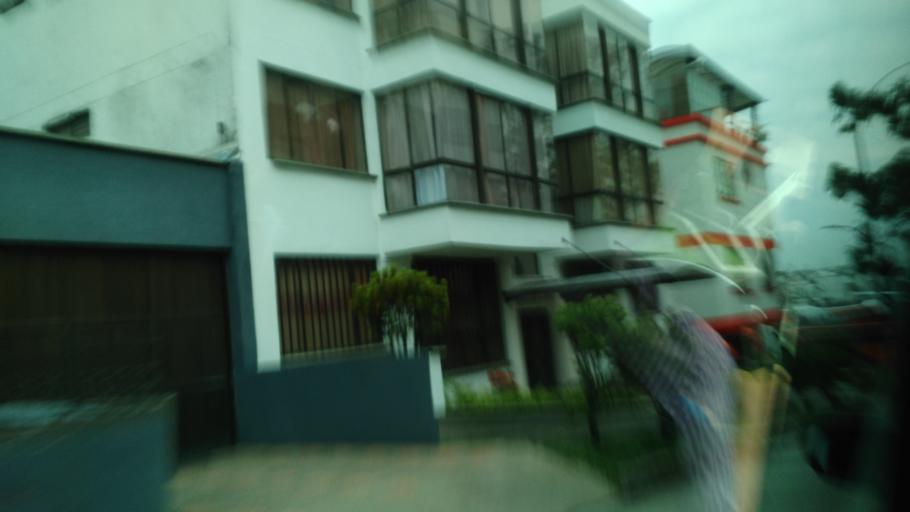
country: CO
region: Risaralda
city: Pereira
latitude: 4.7952
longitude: -75.6916
